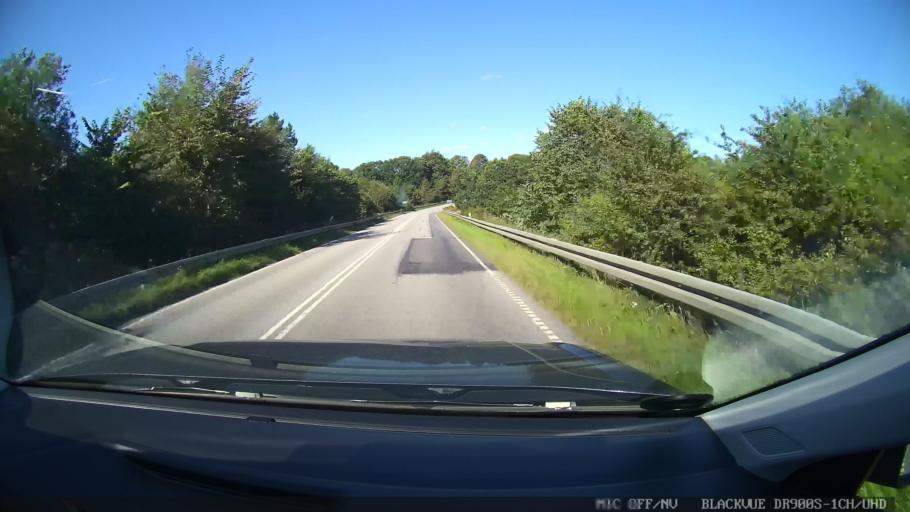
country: DK
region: North Denmark
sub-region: Mariagerfjord Kommune
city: Mariager
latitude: 56.5983
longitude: 9.9987
